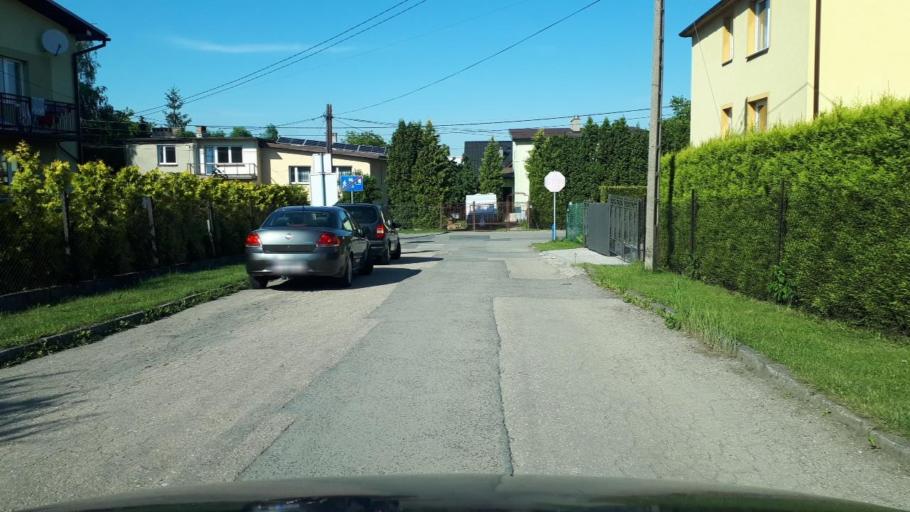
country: PL
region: Silesian Voivodeship
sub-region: Powiat bielski
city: Kozy
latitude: 49.8471
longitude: 19.1507
